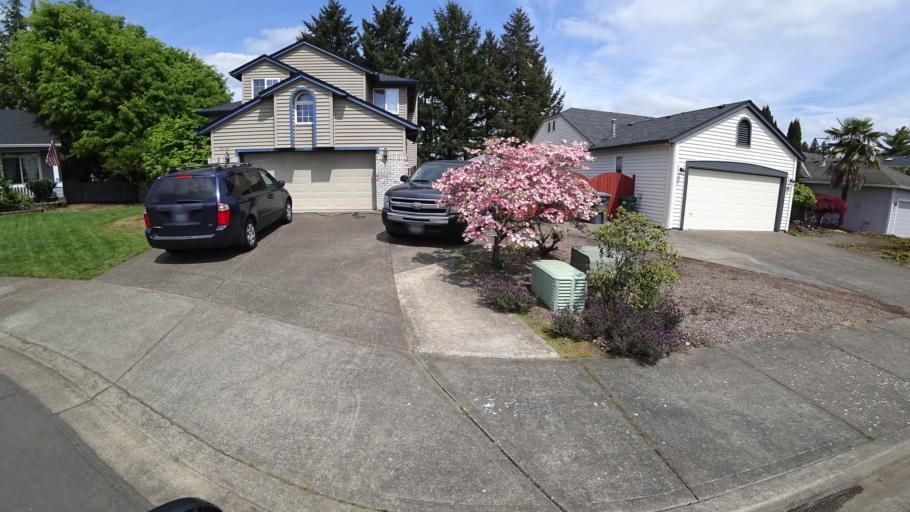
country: US
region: Oregon
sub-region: Washington County
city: Hillsboro
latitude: 45.5400
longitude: -122.9950
